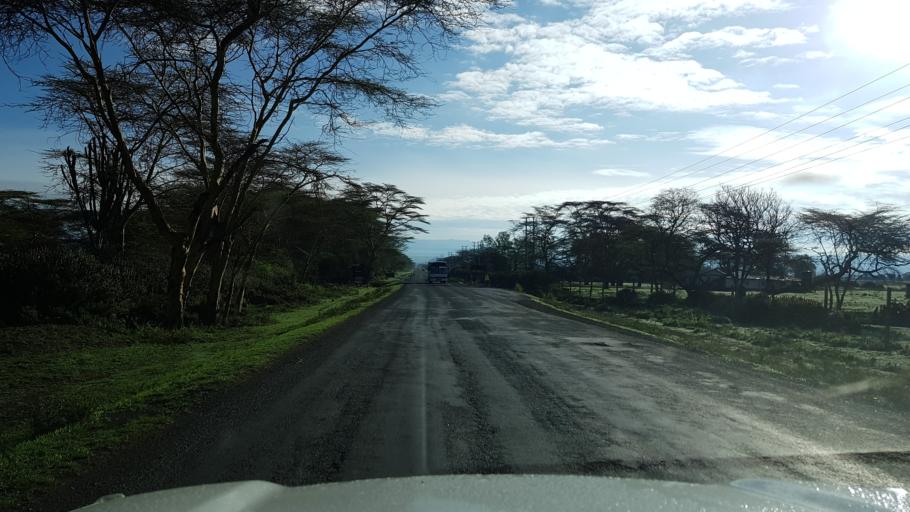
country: KE
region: Nakuru
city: Naivasha
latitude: -0.8151
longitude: 36.3967
